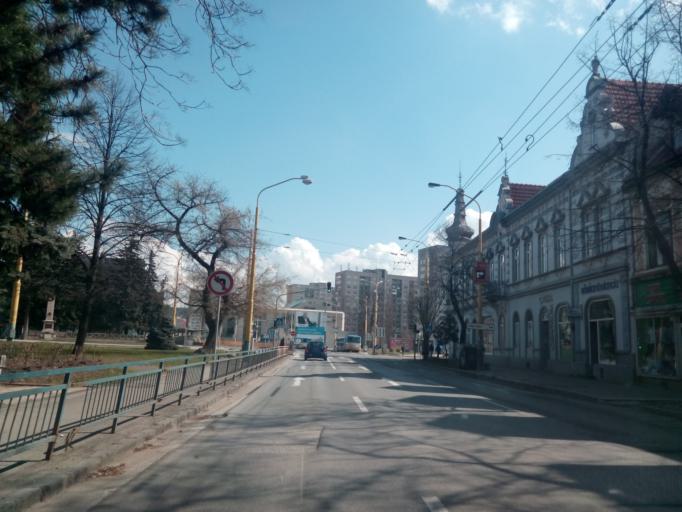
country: SK
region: Kosicky
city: Kosice
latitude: 48.7165
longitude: 21.2597
